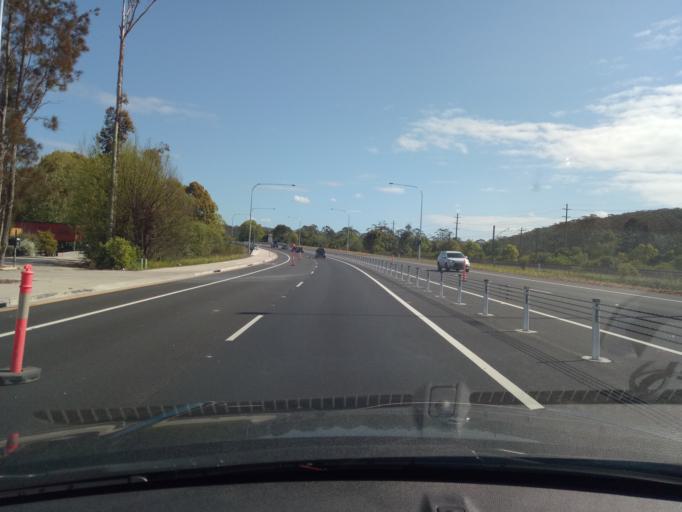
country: AU
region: New South Wales
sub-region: Gosford Shire
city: Lisarow
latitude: -33.3690
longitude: 151.3759
